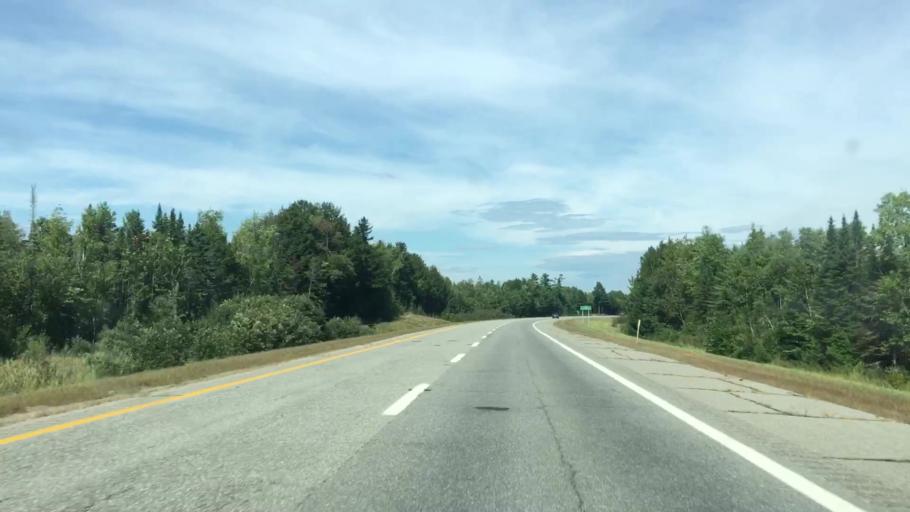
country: US
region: Maine
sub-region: Penobscot County
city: Howland
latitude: 45.3096
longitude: -68.6586
